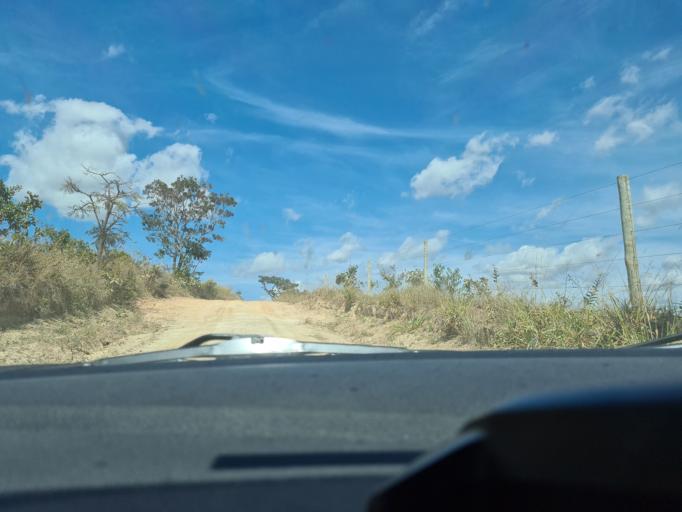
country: BR
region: Goias
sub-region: Silvania
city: Silvania
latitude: -16.5350
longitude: -48.5544
